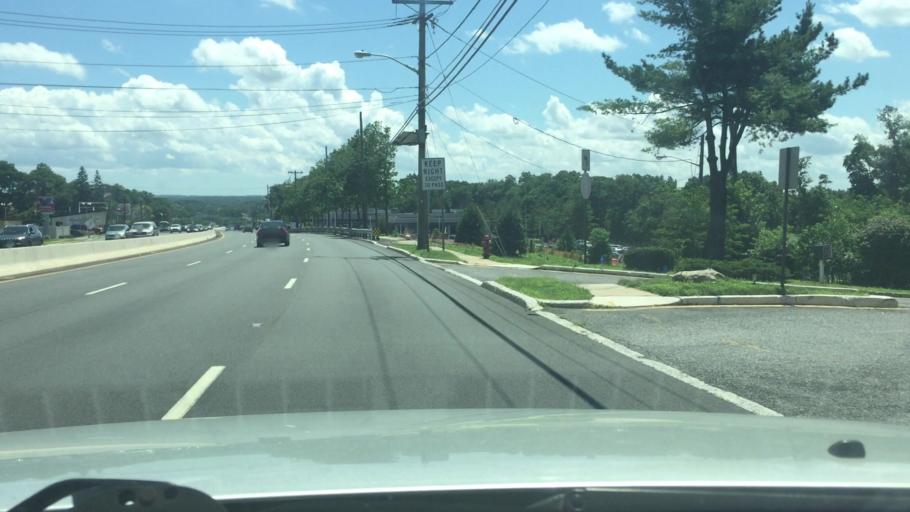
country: US
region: New Jersey
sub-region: Middlesex County
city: Old Bridge
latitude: 40.4192
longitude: -74.3749
